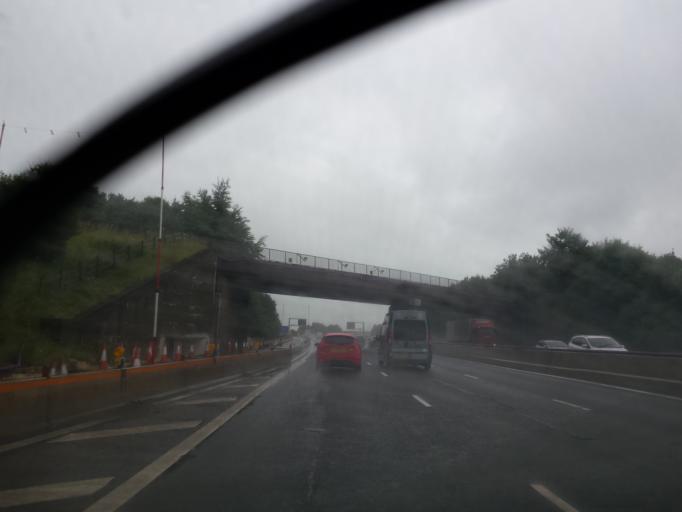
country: GB
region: England
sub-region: Derbyshire
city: Tibshelf
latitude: 53.1362
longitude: -1.3303
